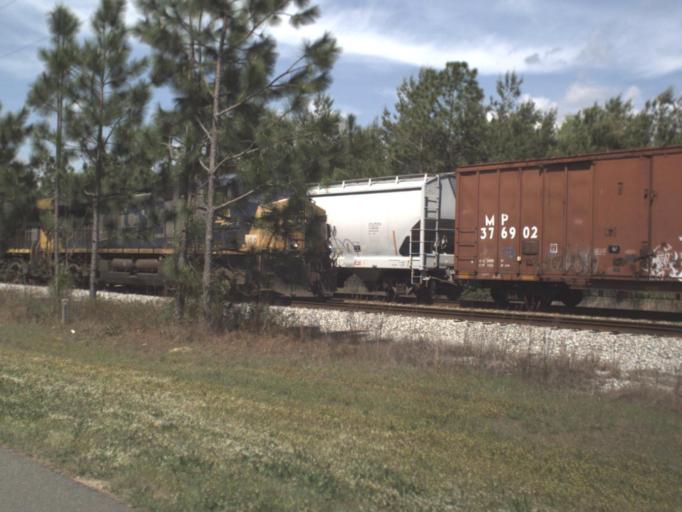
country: US
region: Florida
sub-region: Santa Rosa County
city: East Milton
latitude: 30.6801
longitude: -86.8423
